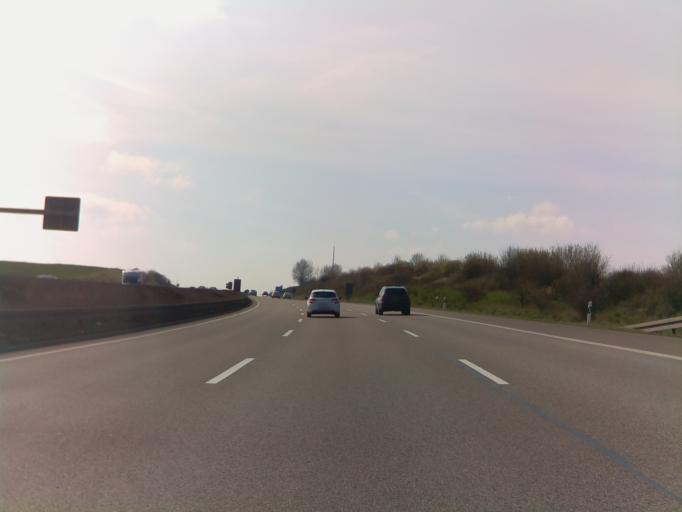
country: DE
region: Thuringia
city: Oettern
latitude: 50.9383
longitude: 11.3679
